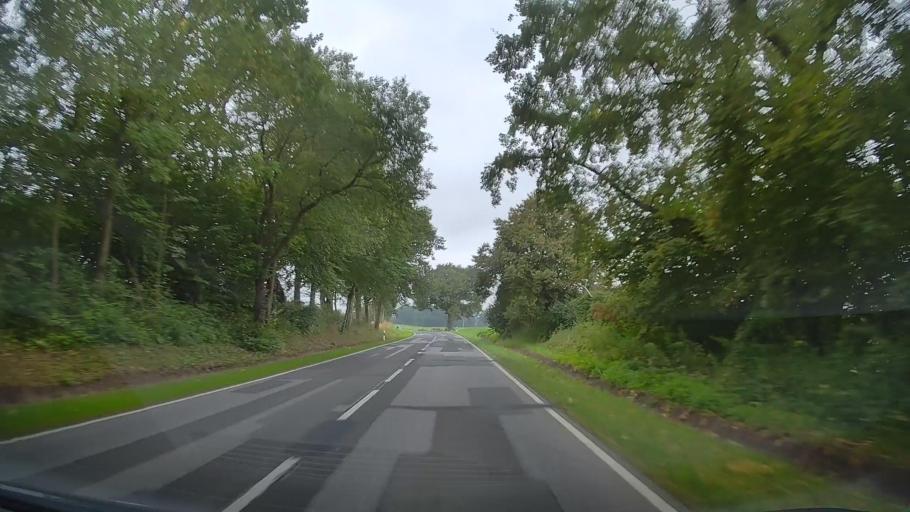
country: DE
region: Mecklenburg-Vorpommern
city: Guestrow
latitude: 53.8369
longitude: 12.1550
